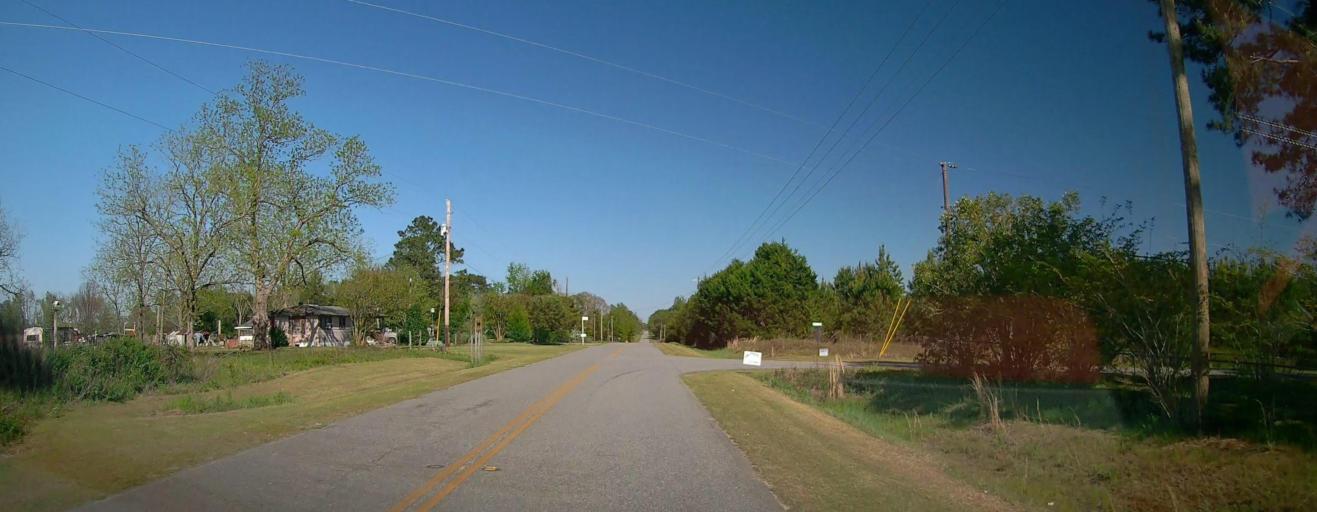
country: US
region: Georgia
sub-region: Pulaski County
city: Hawkinsville
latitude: 32.2477
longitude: -83.4857
